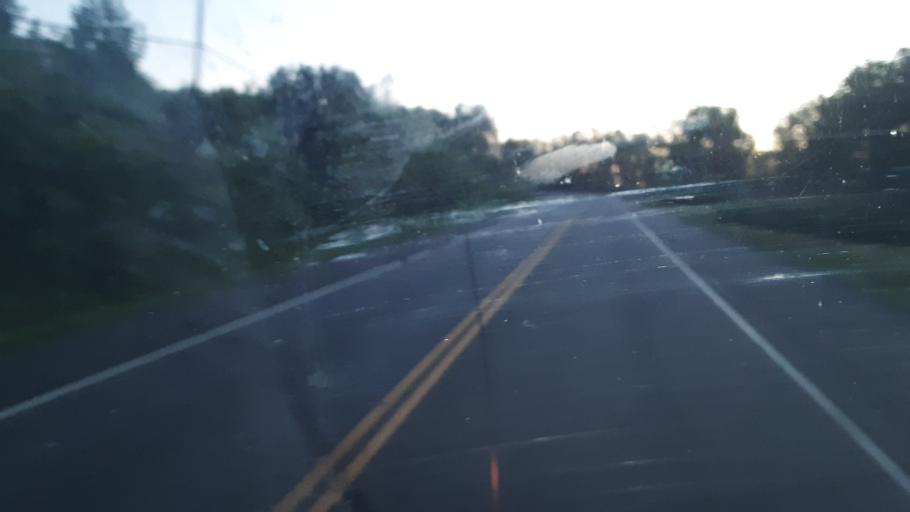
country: US
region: New York
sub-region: Montgomery County
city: Hagaman
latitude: 42.9551
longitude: -74.1140
